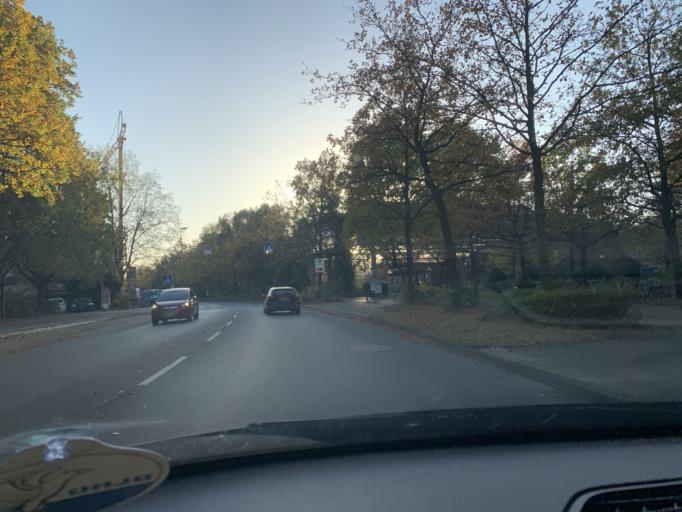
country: DE
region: Lower Saxony
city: Oldenburg
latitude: 53.1471
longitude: 8.1804
